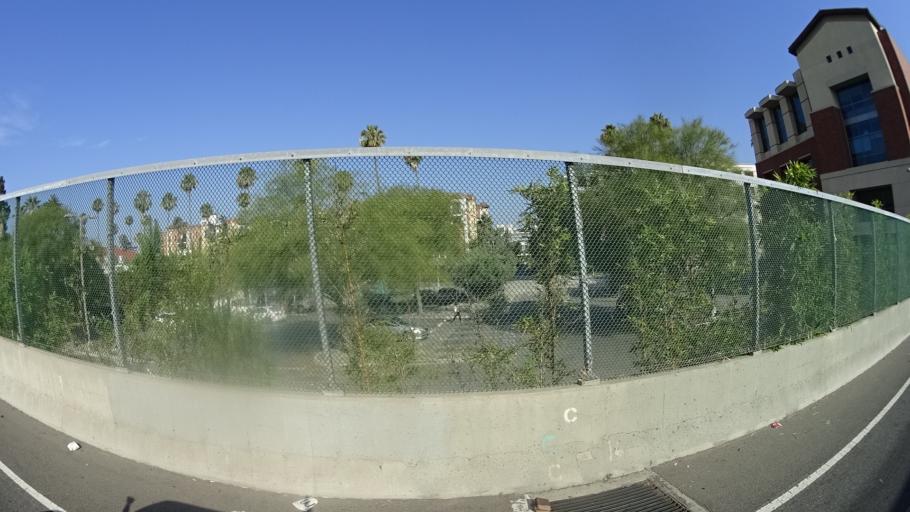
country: US
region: California
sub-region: Los Angeles County
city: Los Angeles
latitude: 34.0170
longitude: -118.2810
